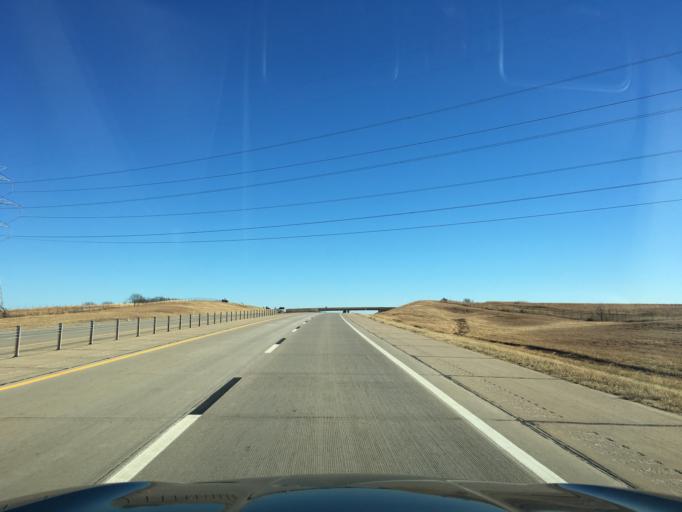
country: US
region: Oklahoma
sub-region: Noble County
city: Perry
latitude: 36.3920
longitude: -97.1088
